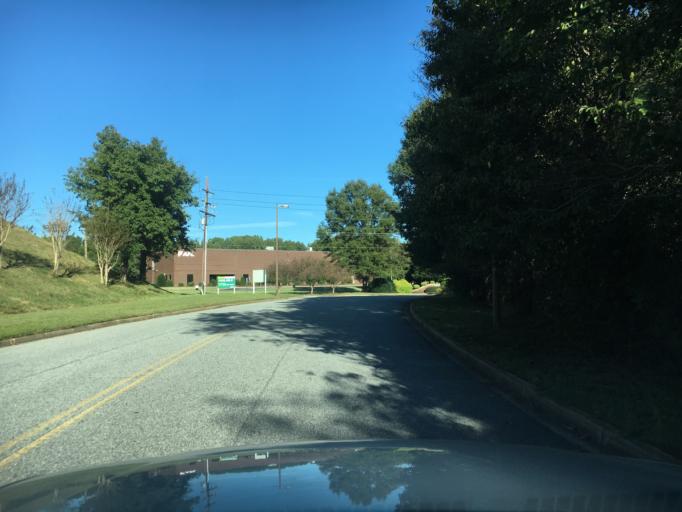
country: US
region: South Carolina
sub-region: Spartanburg County
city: Wellford
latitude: 34.9138
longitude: -82.0990
